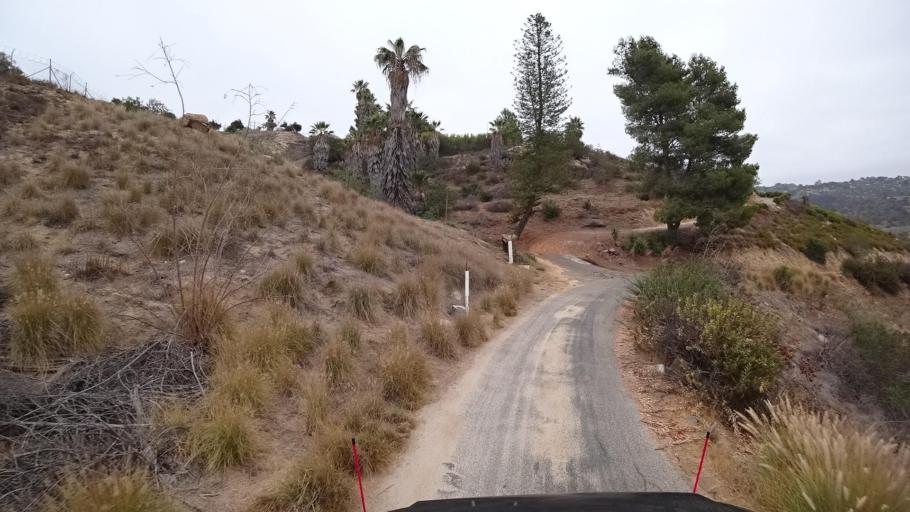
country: US
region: California
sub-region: San Diego County
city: Fallbrook
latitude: 33.4439
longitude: -117.2917
